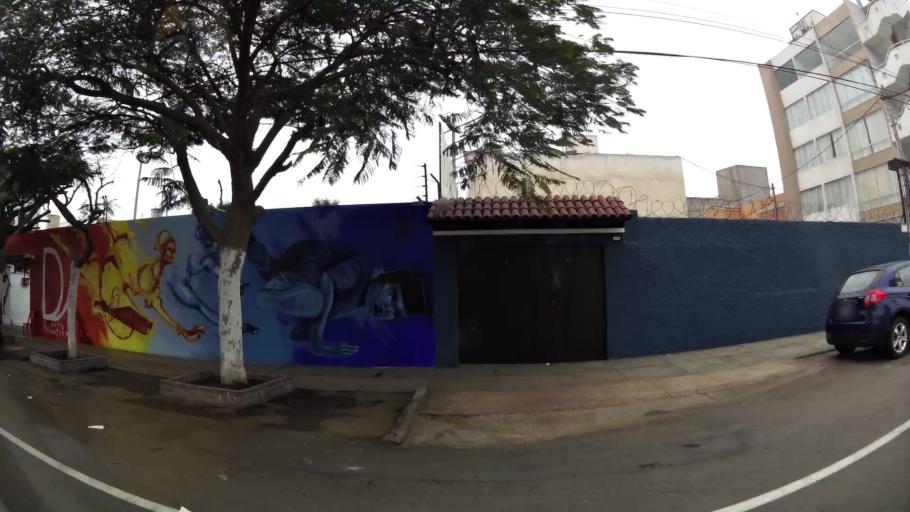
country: PE
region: Lima
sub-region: Lima
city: Surco
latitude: -12.1628
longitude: -77.0238
